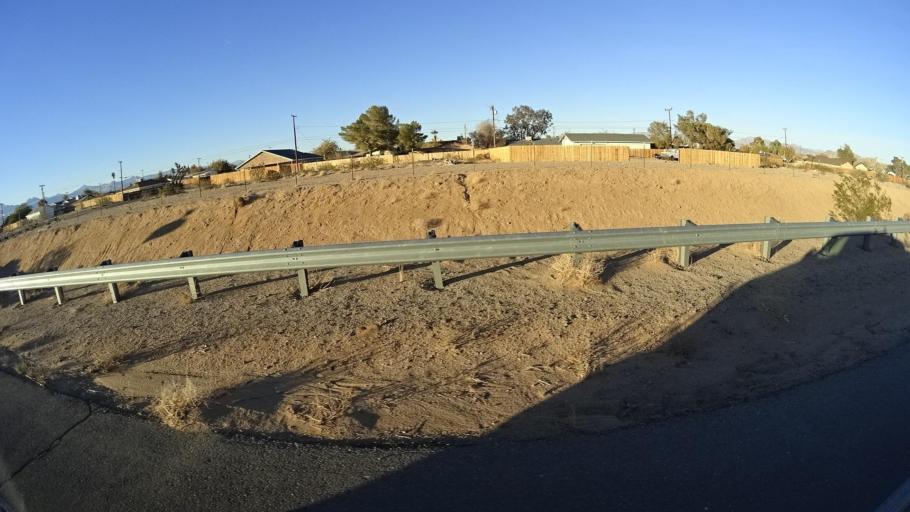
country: US
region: California
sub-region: Kern County
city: Ridgecrest
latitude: 35.6078
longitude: -117.6962
